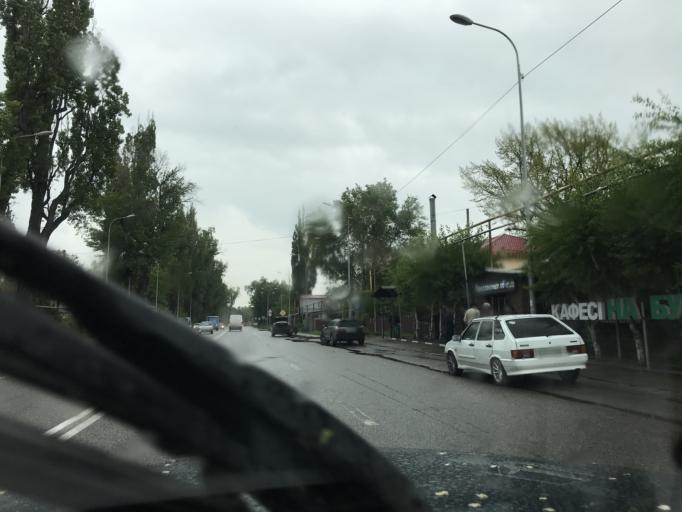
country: KZ
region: Almaty Oblysy
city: Pervomayskiy
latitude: 43.3423
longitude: 76.9669
